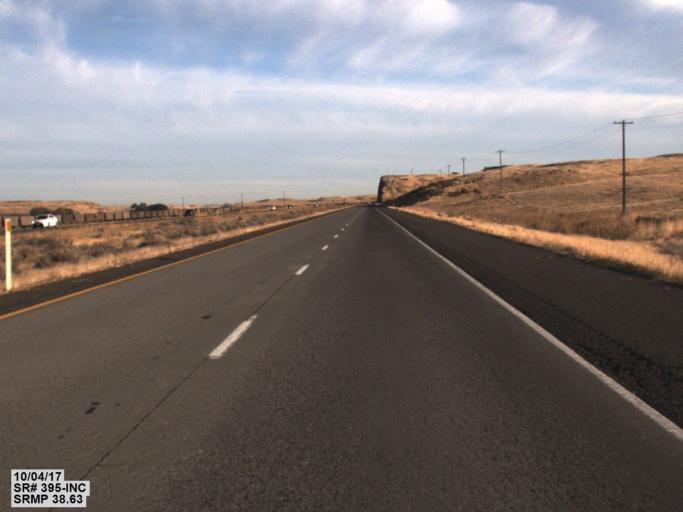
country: US
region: Washington
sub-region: Franklin County
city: Basin City
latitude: 46.4661
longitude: -119.0122
